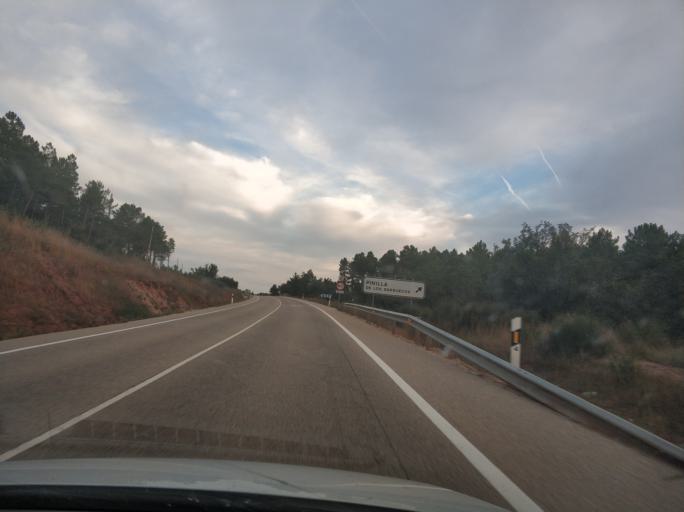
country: ES
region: Castille and Leon
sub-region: Provincia de Burgos
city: Pinilla de los Barruecos
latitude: 41.9445
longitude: -3.2916
